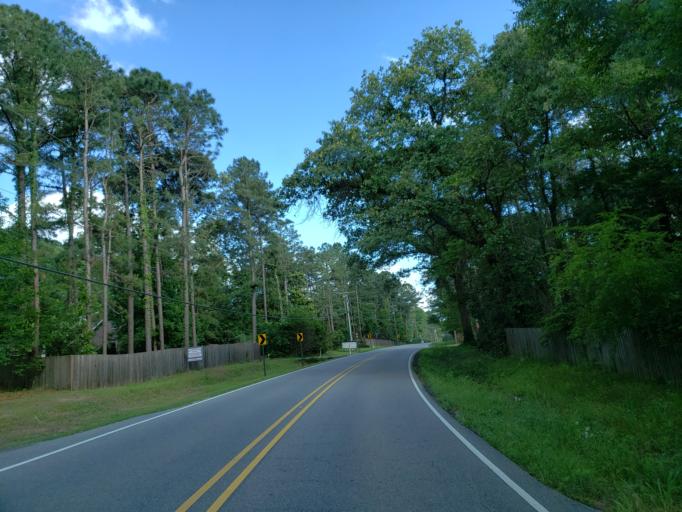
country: US
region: Mississippi
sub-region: Lamar County
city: West Hattiesburg
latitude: 31.2849
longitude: -89.4374
